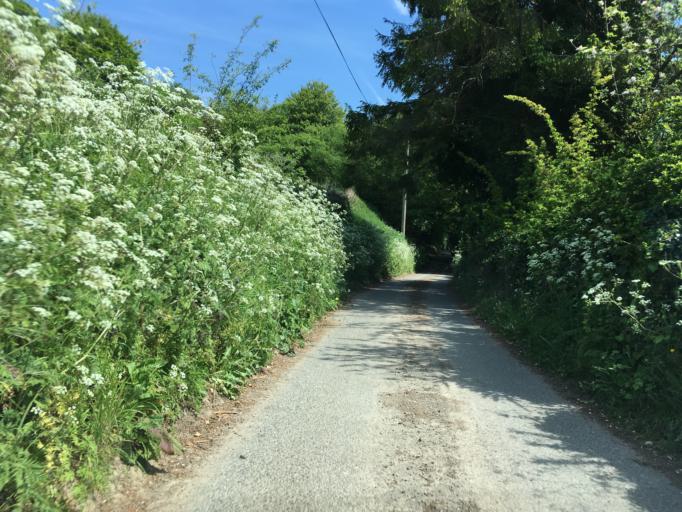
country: GB
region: England
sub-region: Gloucestershire
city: Dursley
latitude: 51.6621
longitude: -2.3488
